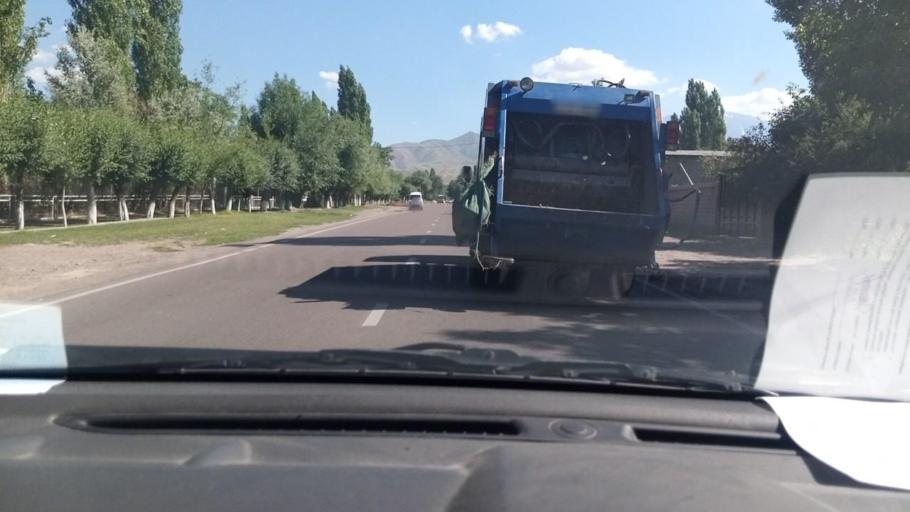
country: UZ
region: Toshkent
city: Angren
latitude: 41.0297
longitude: 70.0906
